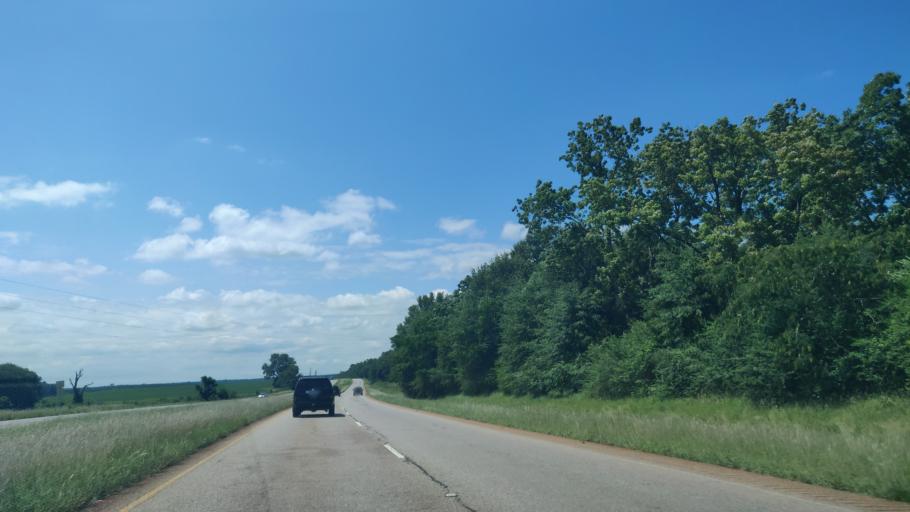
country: US
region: Georgia
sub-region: Stewart County
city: Richland
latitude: 32.0709
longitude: -84.6717
